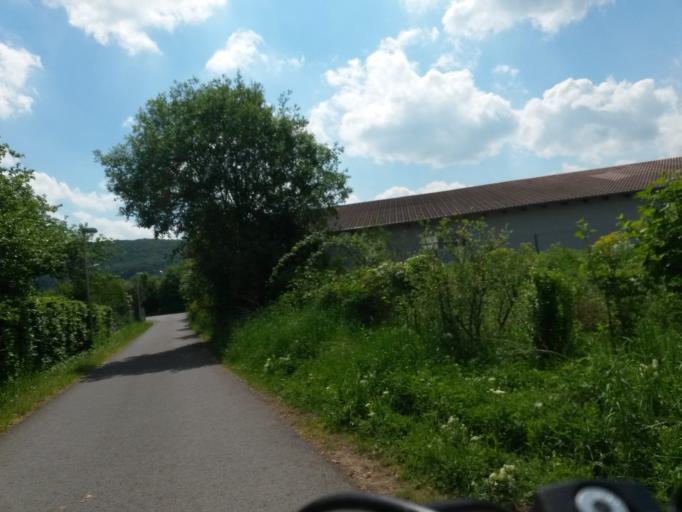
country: DE
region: Bavaria
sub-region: Regierungsbezirk Unterfranken
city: Euerdorf
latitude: 50.1507
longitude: 10.0181
